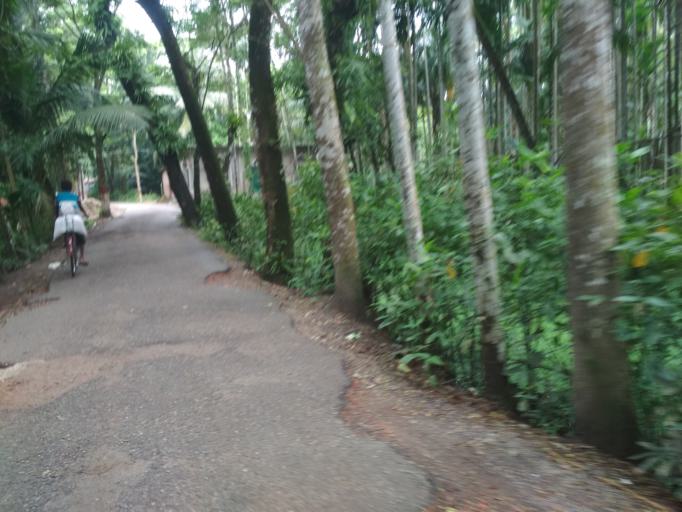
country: BD
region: Chittagong
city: Lakshmipur
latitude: 22.9666
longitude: 90.8041
